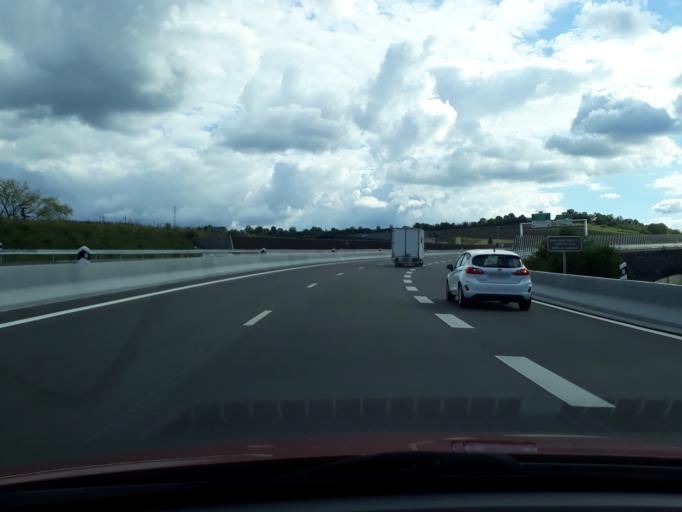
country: FR
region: Auvergne
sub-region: Departement de la Haute-Loire
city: Chadrac
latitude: 45.0529
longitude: 3.9068
